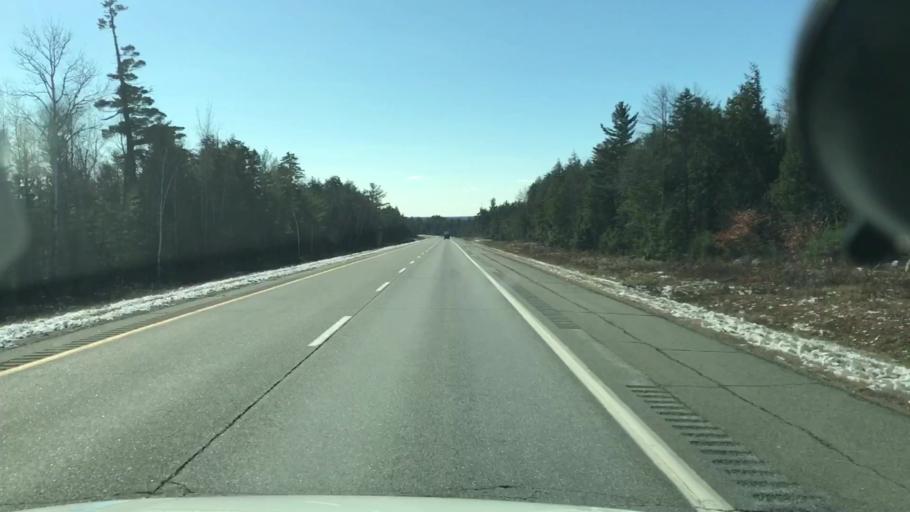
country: US
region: Maine
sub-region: Penobscot County
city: Howland
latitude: 45.2803
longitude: -68.6723
